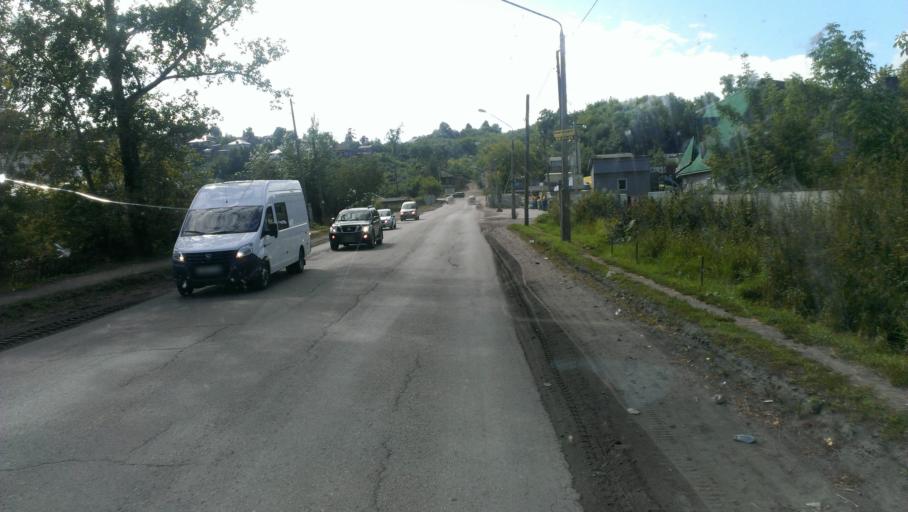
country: RU
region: Altai Krai
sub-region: Gorod Barnaulskiy
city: Barnaul
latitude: 53.3209
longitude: 83.7694
